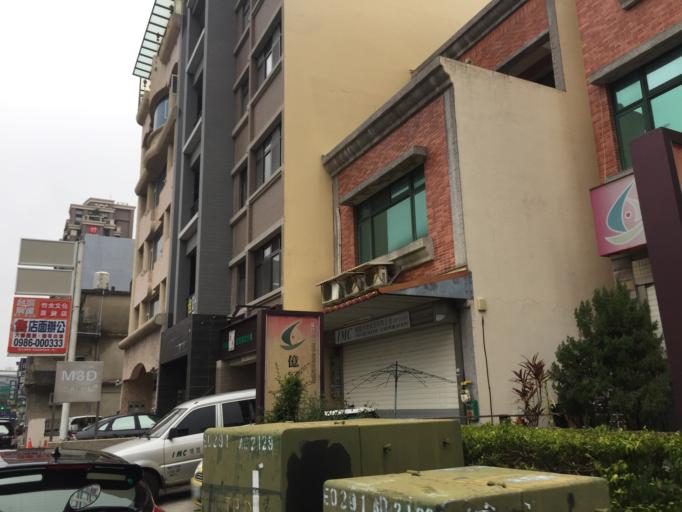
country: TW
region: Taiwan
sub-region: Hsinchu
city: Zhubei
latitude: 24.8178
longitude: 121.0243
